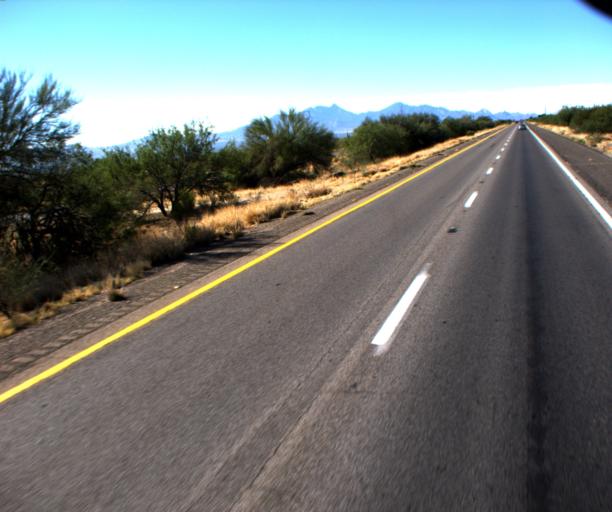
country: US
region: Arizona
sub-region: Pima County
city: Sahuarita
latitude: 31.9813
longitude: -110.9911
